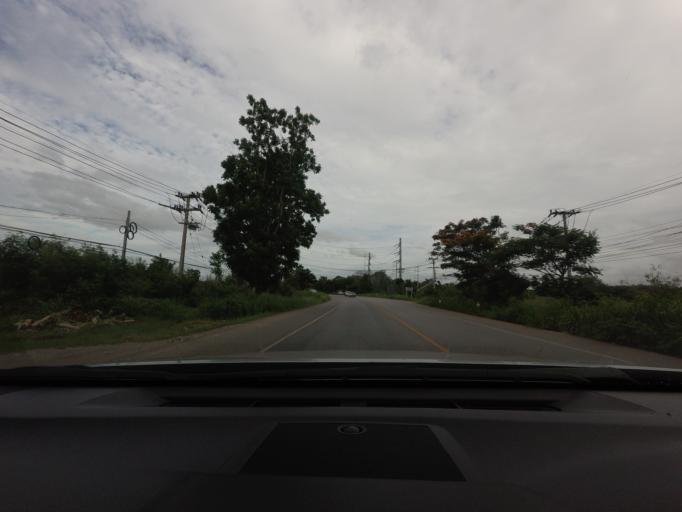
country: TH
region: Prachuap Khiri Khan
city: Hua Hin
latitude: 12.5781
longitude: 99.8617
